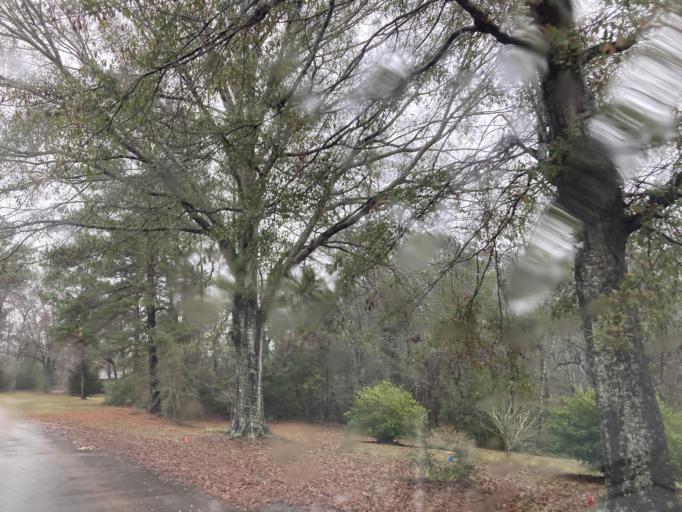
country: US
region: Mississippi
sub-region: Forrest County
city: Rawls Springs
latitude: 31.4945
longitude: -89.3616
